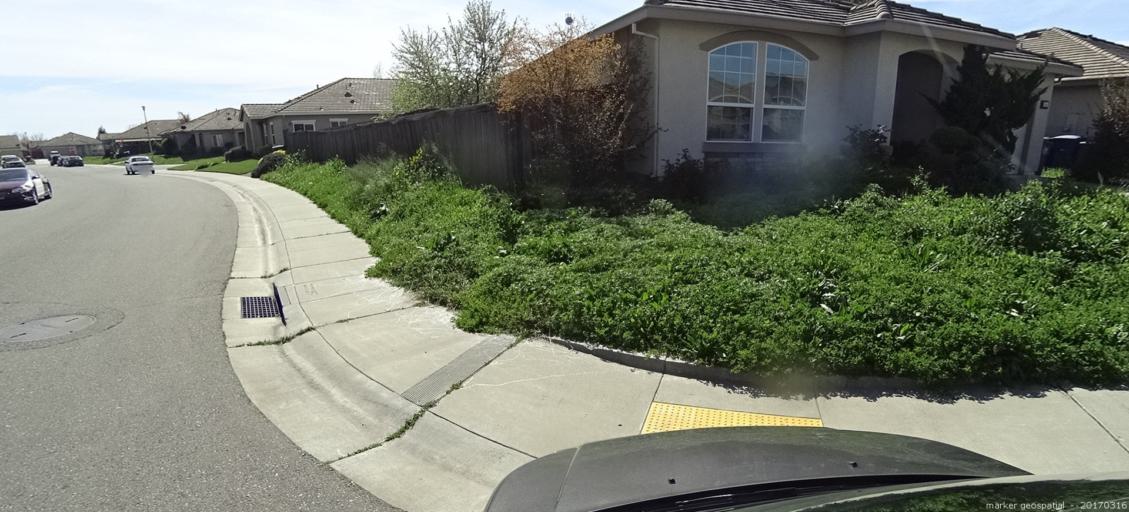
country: US
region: California
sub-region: Sacramento County
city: Parkway
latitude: 38.4758
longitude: -121.4939
